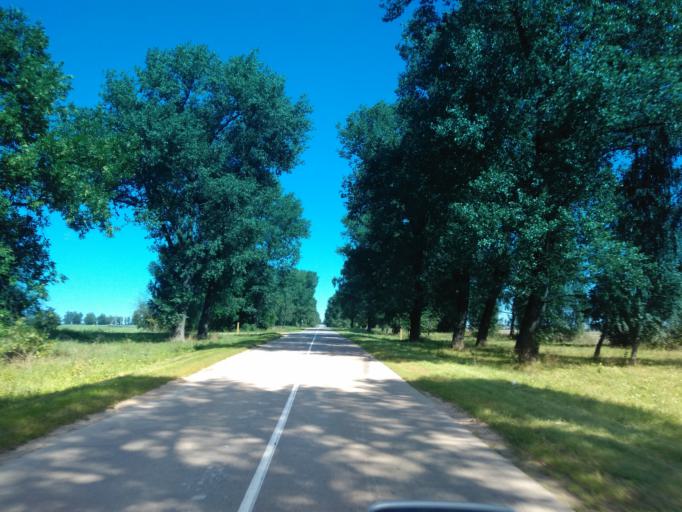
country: BY
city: Fanipol
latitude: 53.6756
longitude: 27.3529
